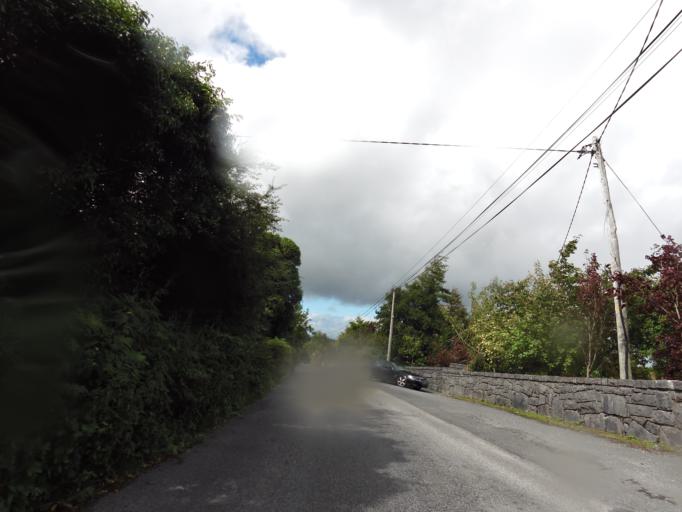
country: IE
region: Connaught
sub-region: County Galway
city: Oughterard
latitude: 53.4190
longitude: -9.3290
